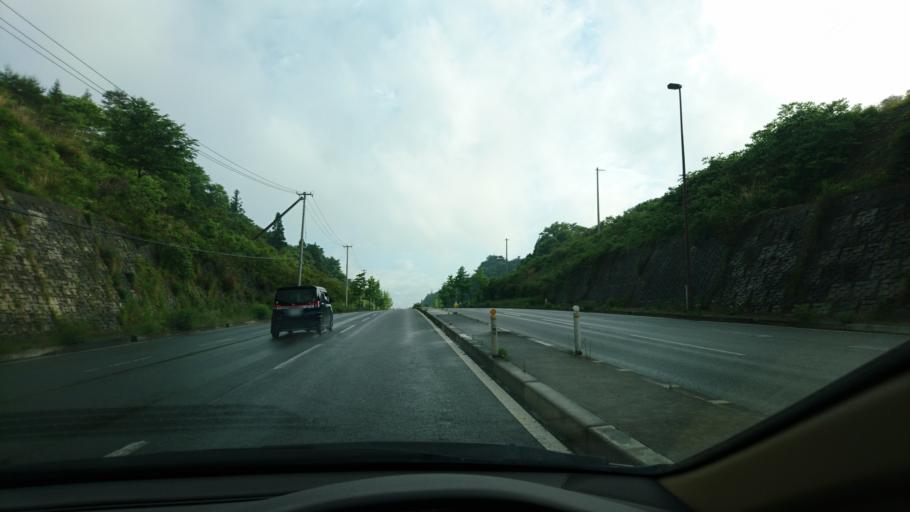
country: JP
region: Iwate
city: Ichinoseki
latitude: 38.9302
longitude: 141.1658
